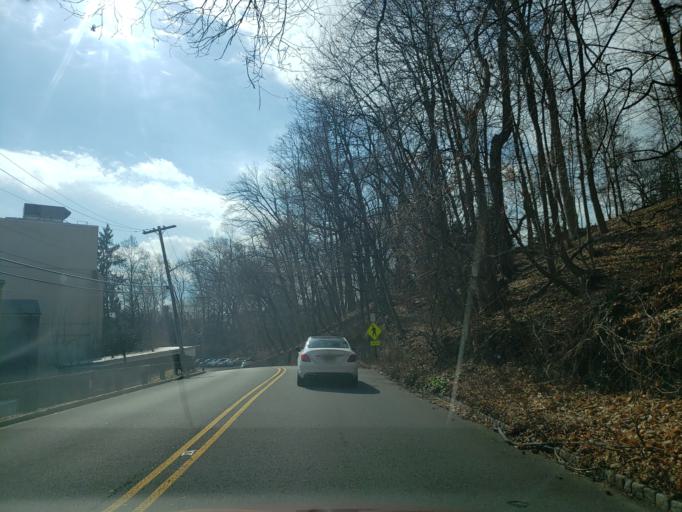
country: US
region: New Jersey
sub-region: Essex County
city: Short Hills
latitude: 40.7289
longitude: -74.3093
